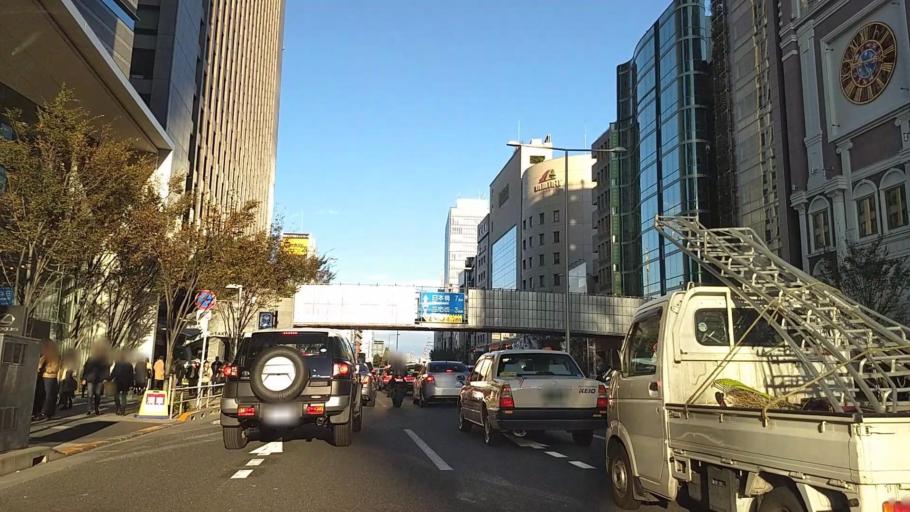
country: JP
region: Tokyo
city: Tokyo
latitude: 35.6707
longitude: 139.7188
